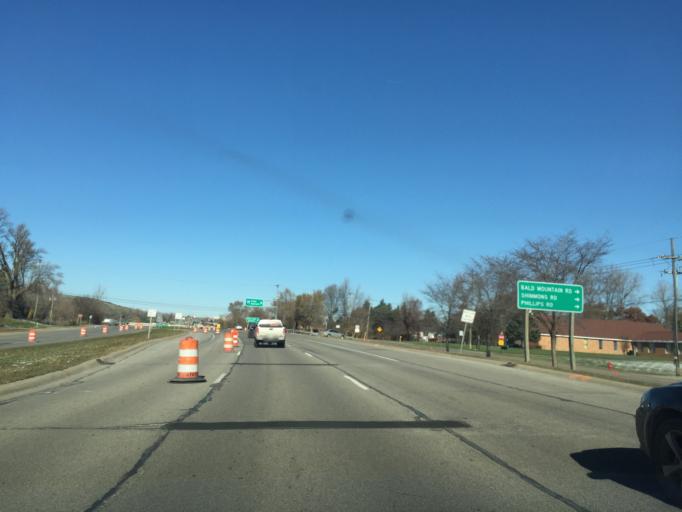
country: US
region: Michigan
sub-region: Oakland County
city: Auburn Hills
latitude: 42.6877
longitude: -83.2408
